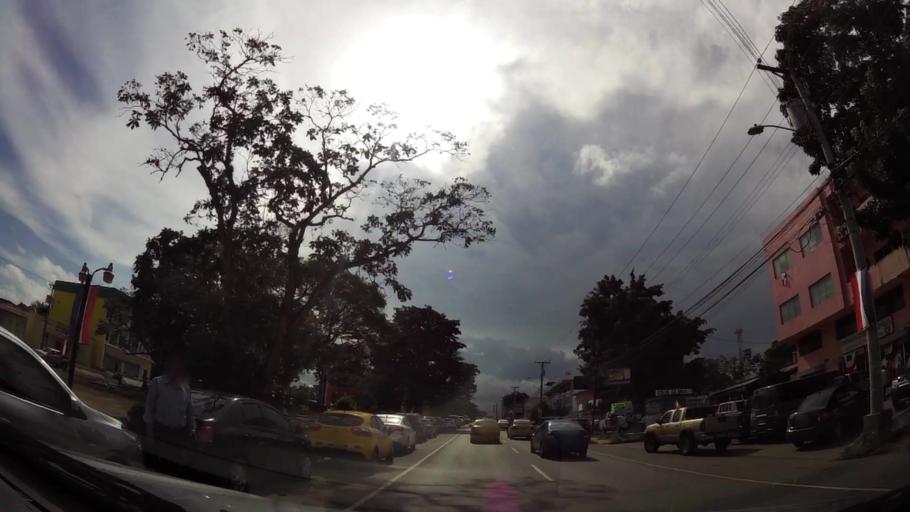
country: PA
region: Panama
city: La Chorrera
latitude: 8.8759
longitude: -79.7881
